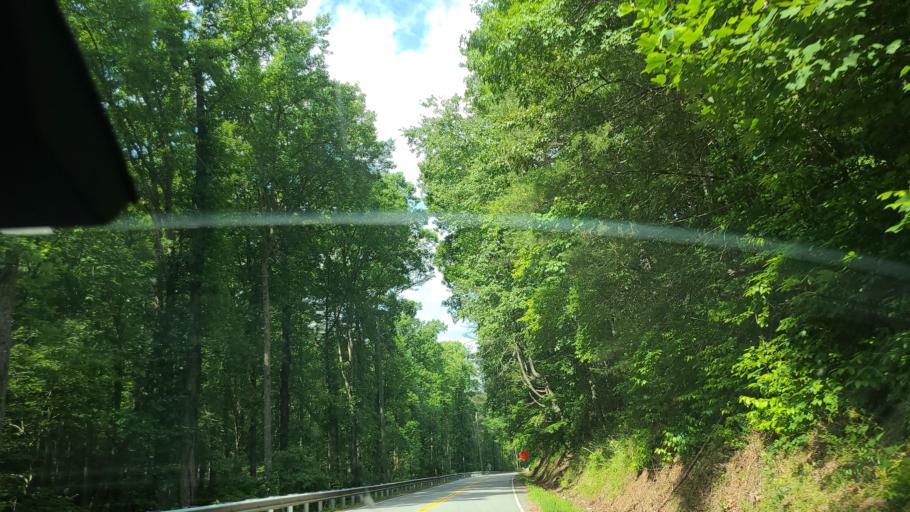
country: US
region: South Carolina
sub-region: Oconee County
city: Walhalla
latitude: 34.8679
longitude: -83.1560
